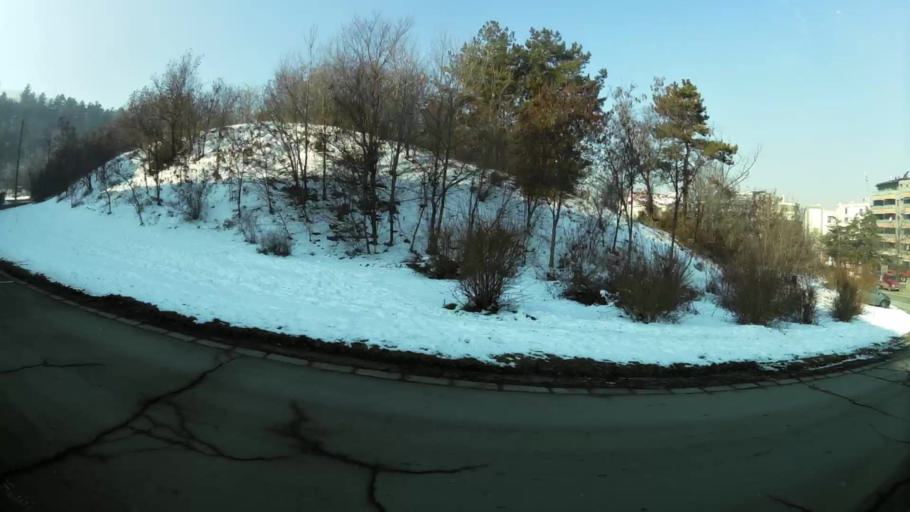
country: MK
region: Karpos
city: Skopje
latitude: 41.9823
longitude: 21.4218
